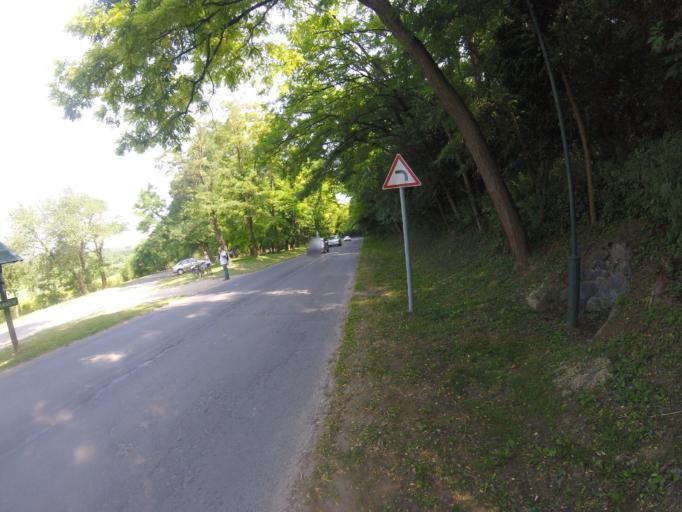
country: HU
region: Veszprem
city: Tapolca
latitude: 46.8058
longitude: 17.4341
